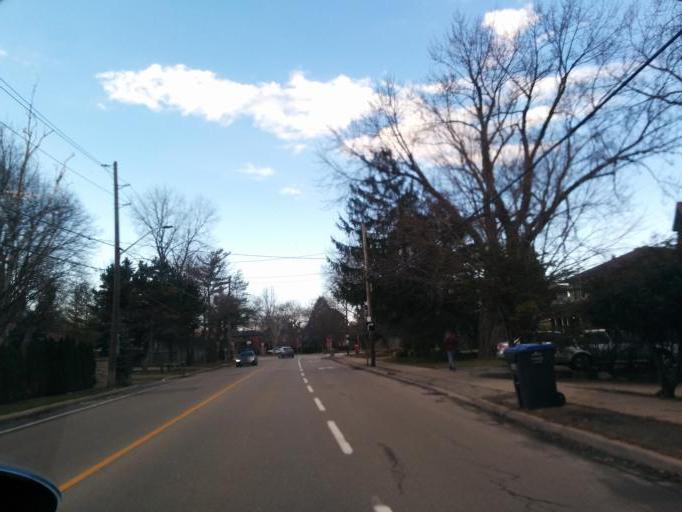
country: CA
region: Ontario
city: Mississauga
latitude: 43.5356
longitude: -79.6275
